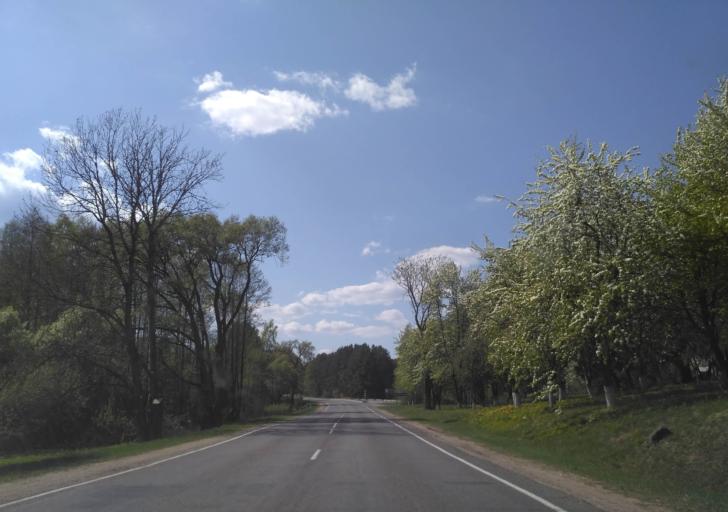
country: BY
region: Minsk
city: Narach
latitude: 54.8867
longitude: 26.8125
